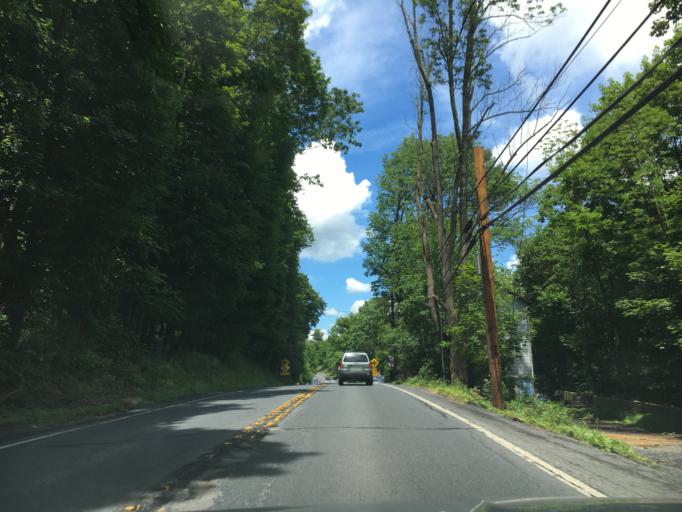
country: US
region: Pennsylvania
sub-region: Lehigh County
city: Laurys Station
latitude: 40.7196
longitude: -75.5268
